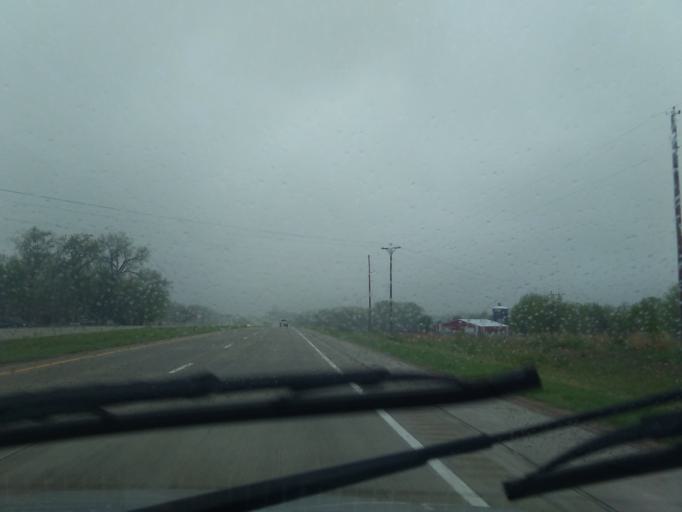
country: US
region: Nebraska
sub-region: Madison County
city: Norfolk
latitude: 42.0628
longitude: -97.3493
